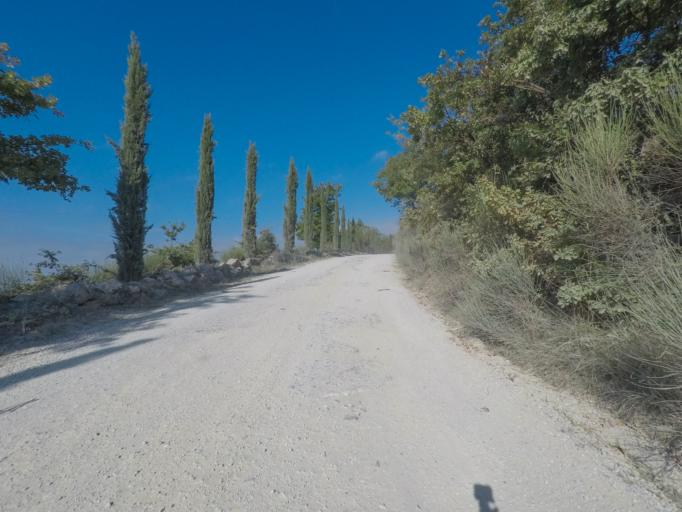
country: IT
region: Tuscany
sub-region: Provincia di Siena
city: Castellina in Chianti
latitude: 43.4359
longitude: 11.3299
